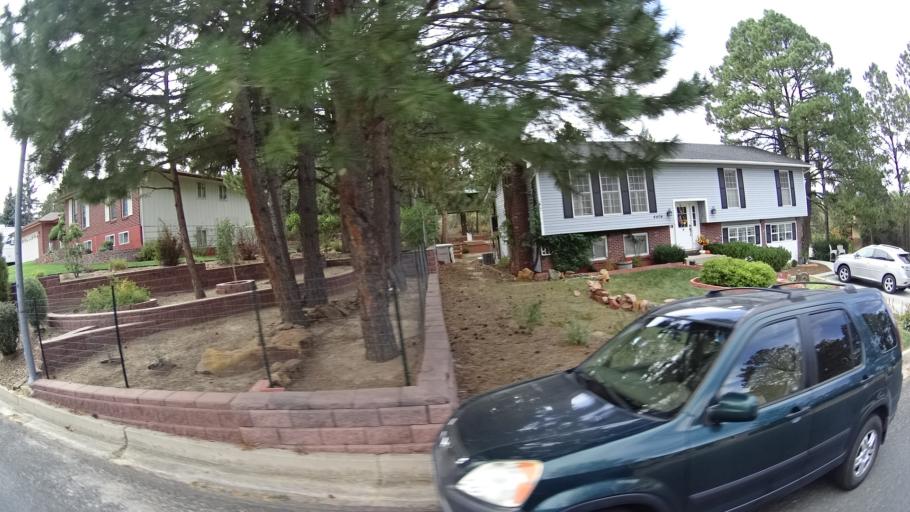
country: US
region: Colorado
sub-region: El Paso County
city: Colorado Springs
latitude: 38.8972
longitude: -104.7767
